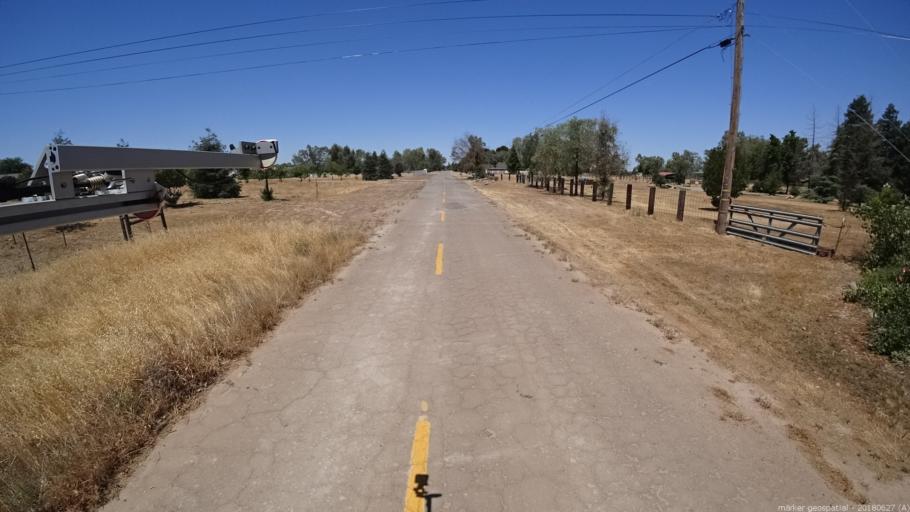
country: US
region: California
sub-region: Madera County
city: Bonadelle Ranchos-Madera Ranchos
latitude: 36.9358
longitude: -119.8590
